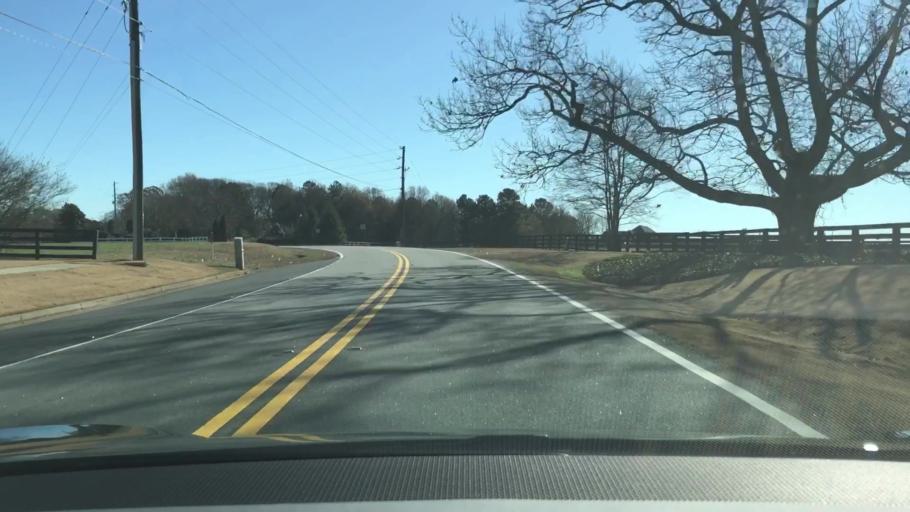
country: US
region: Georgia
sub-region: Walton County
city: Monroe
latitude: 33.8649
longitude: -83.7523
